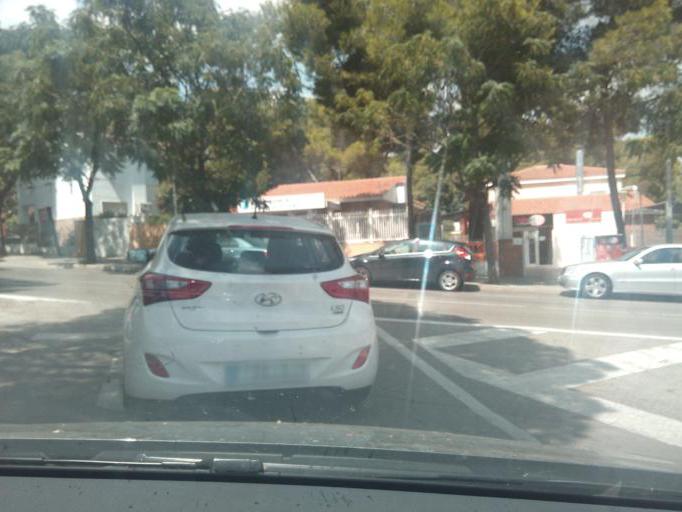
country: ES
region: Valencia
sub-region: Provincia de Valencia
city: Manises
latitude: 39.5288
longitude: -0.4848
